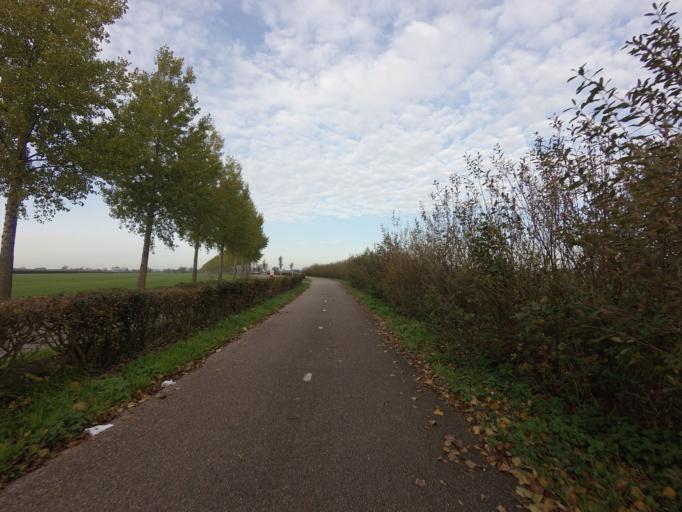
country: NL
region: Utrecht
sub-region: Gemeente IJsselstein
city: IJsselstein
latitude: 52.0017
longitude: 5.0012
